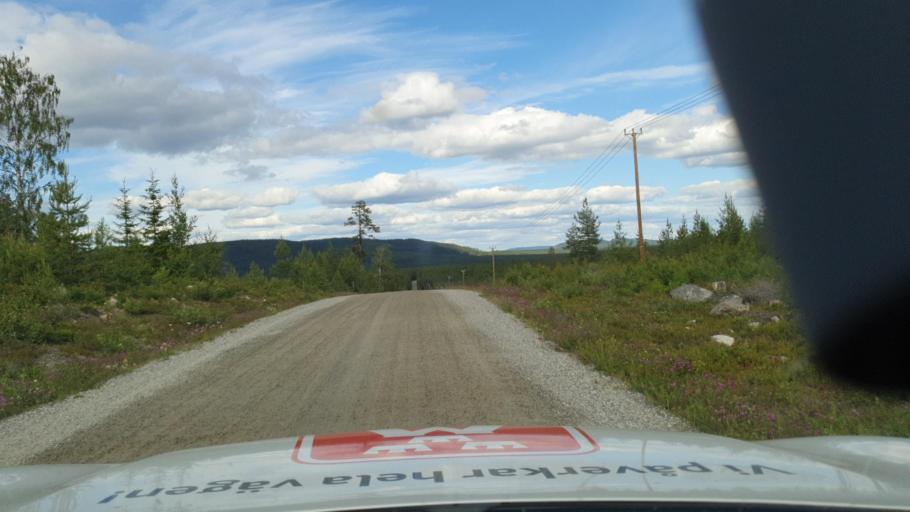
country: SE
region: Vaesterbotten
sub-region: Asele Kommun
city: Insjon
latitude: 64.2332
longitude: 17.8967
